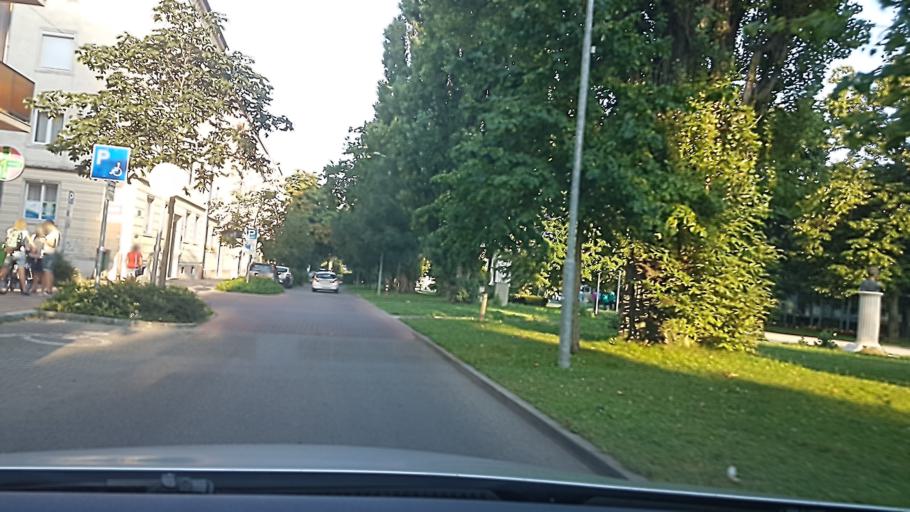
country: HU
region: Gyor-Moson-Sopron
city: Sopron
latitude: 47.6807
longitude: 16.5875
